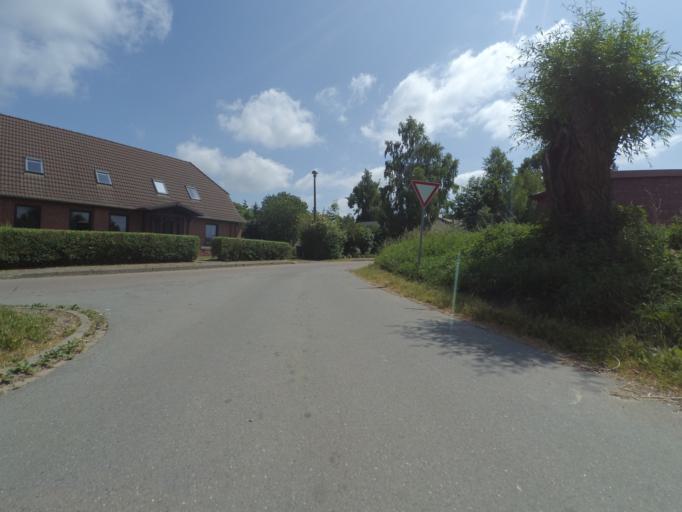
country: DE
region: Mecklenburg-Vorpommern
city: Neuburg
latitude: 53.4763
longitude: 11.9126
